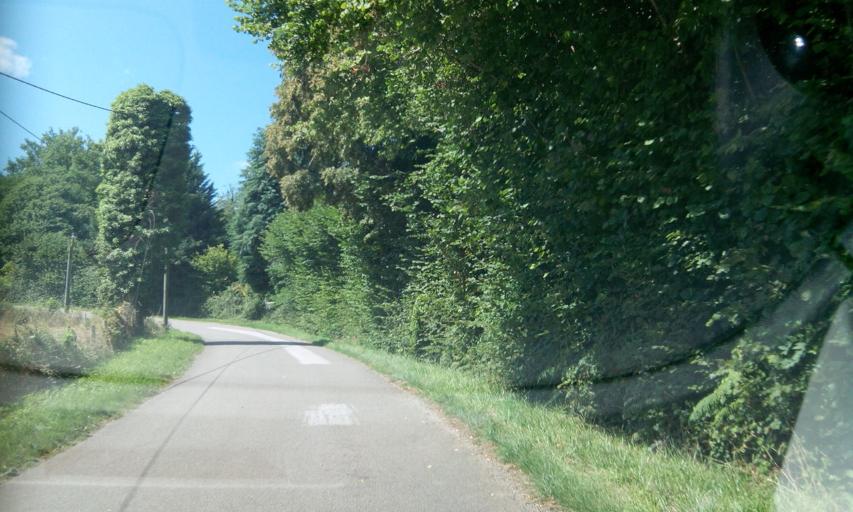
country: FR
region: Limousin
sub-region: Departement de la Haute-Vienne
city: Saint-Leonard-de-Noblat
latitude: 45.8041
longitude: 1.4602
